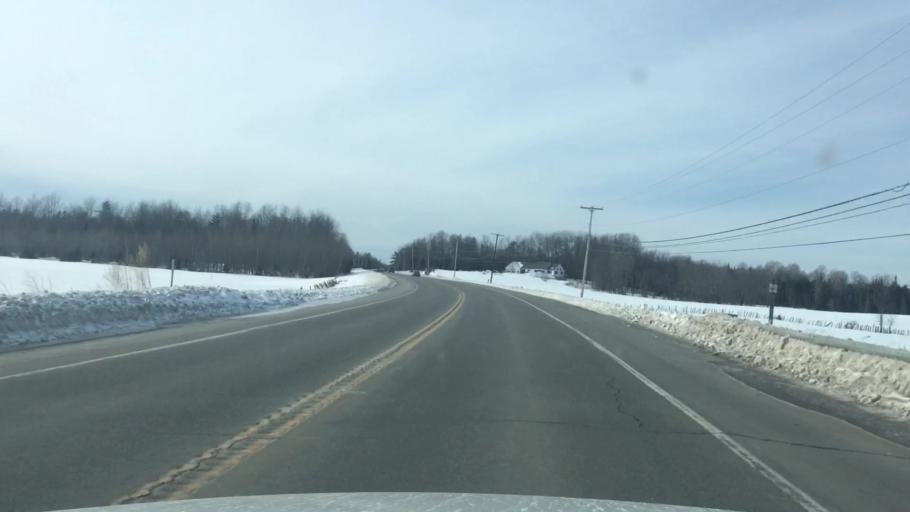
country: US
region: Maine
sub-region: Penobscot County
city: Kenduskeag
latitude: 44.9109
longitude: -68.8993
